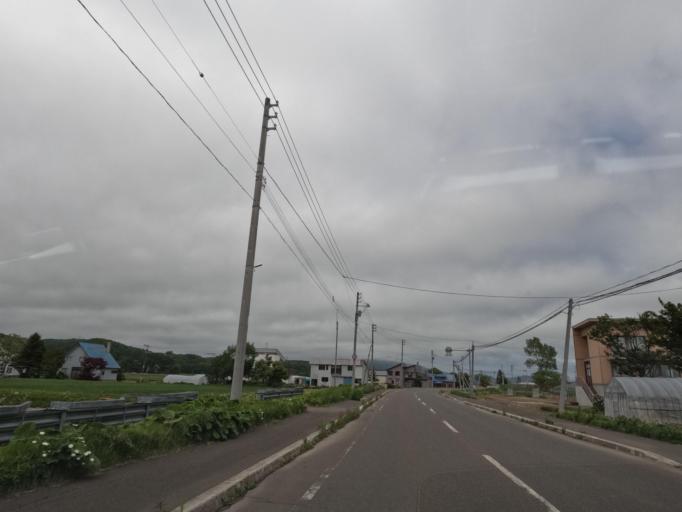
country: JP
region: Hokkaido
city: Tobetsu
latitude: 43.2418
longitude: 141.5137
